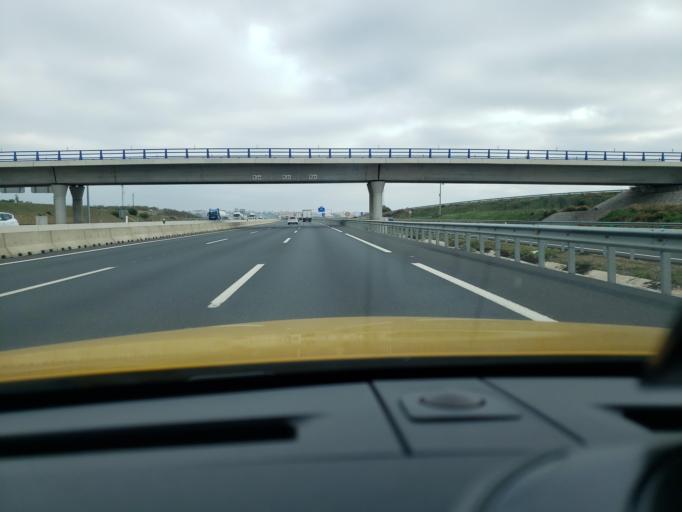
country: ES
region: Andalusia
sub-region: Provincia de Sevilla
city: Espartinas
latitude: 37.3651
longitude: -6.1158
